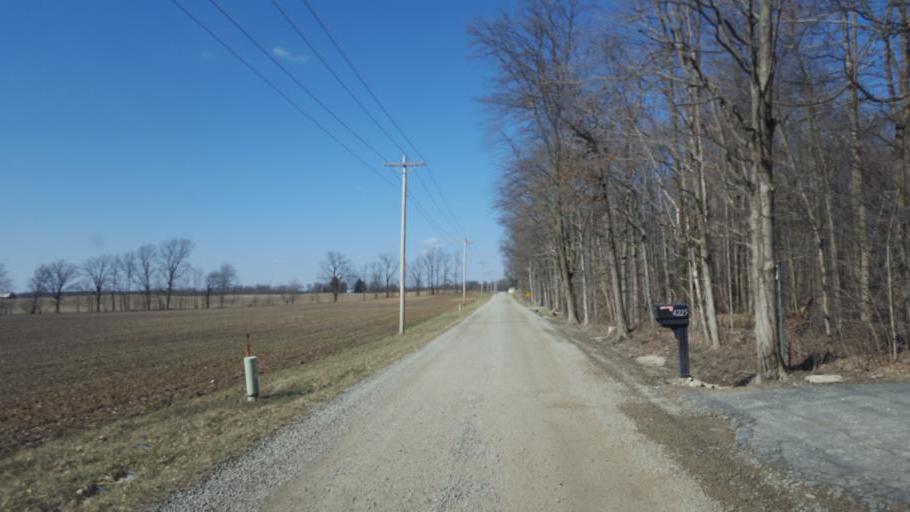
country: US
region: Ohio
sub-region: Morrow County
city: Mount Gilead
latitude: 40.5005
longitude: -82.7719
